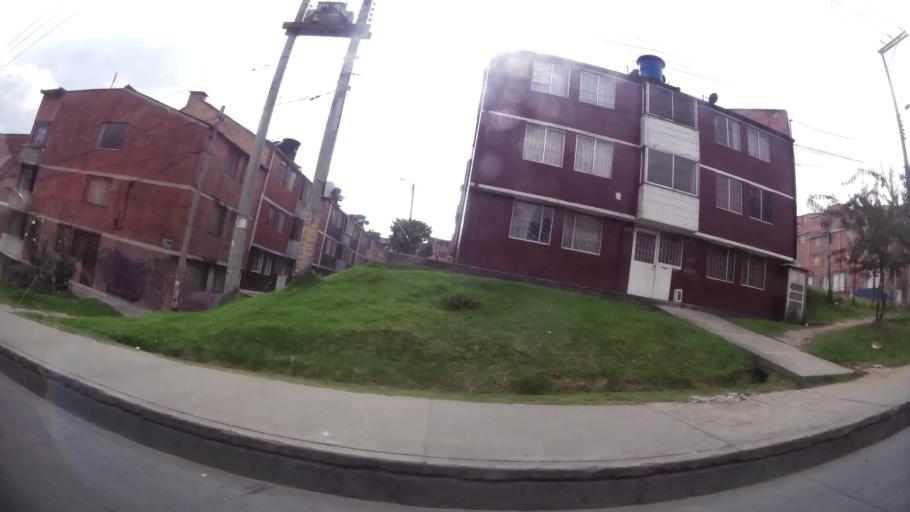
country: CO
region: Bogota D.C.
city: Bogota
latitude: 4.5609
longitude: -74.1108
